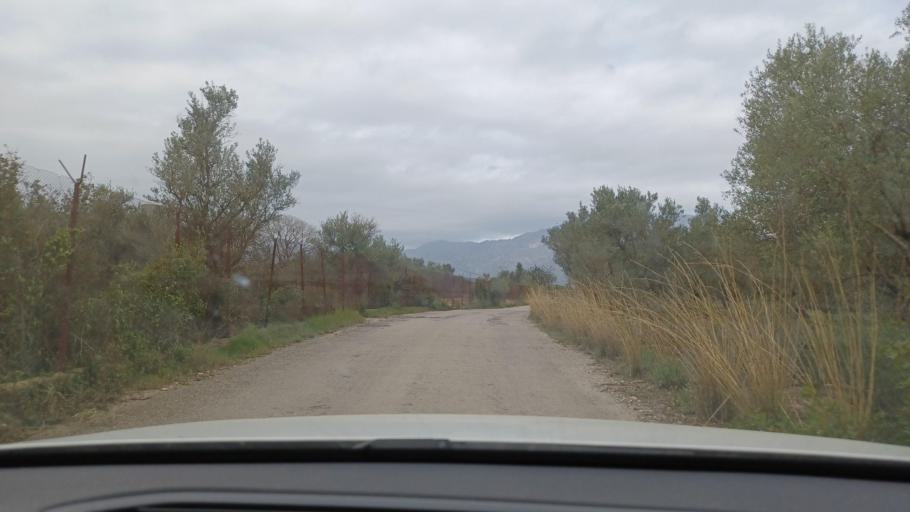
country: ES
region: Catalonia
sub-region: Provincia de Tarragona
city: Tortosa
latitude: 40.7919
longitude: 0.4725
